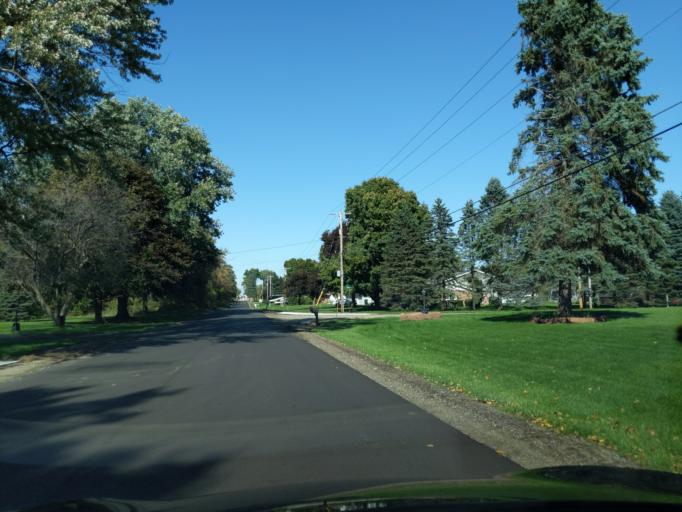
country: US
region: Michigan
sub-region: Eaton County
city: Charlotte
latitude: 42.5838
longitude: -84.7978
